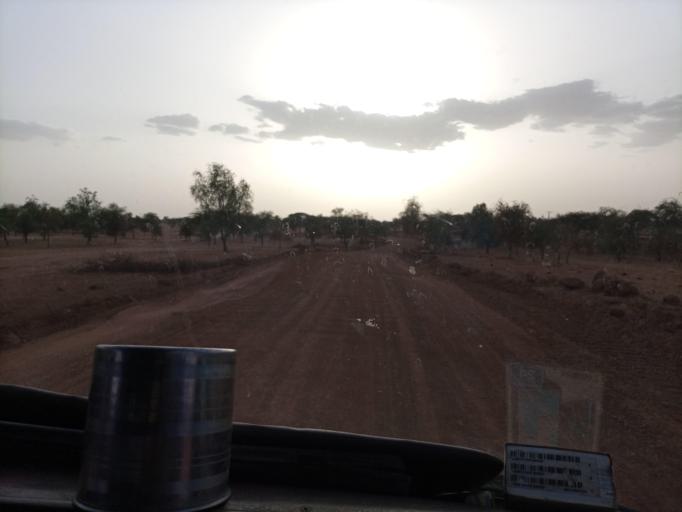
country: SN
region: Louga
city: Dara
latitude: 15.3709
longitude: -15.5796
